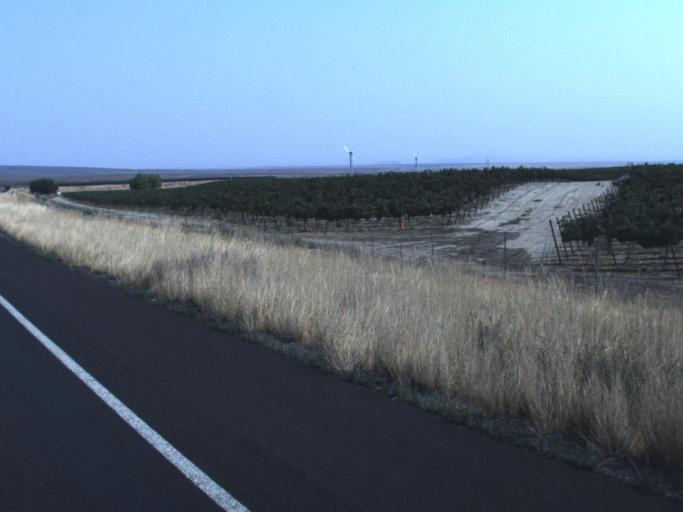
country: US
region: Washington
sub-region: Grant County
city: Desert Aire
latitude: 46.5639
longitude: -119.8020
